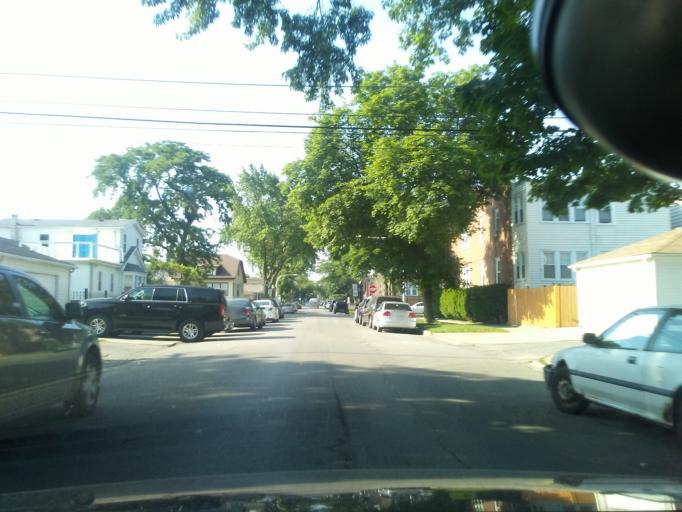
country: US
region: Illinois
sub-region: Cook County
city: Oak Park
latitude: 41.9257
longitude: -87.7513
